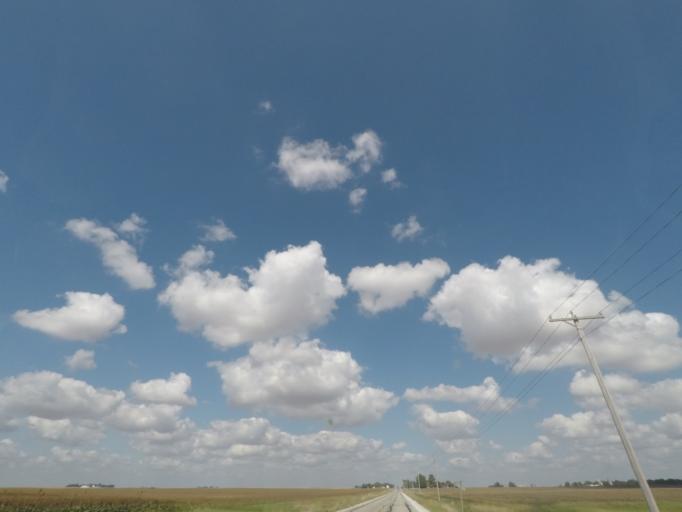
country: US
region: Iowa
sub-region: Story County
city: Nevada
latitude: 42.0556
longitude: -93.4057
